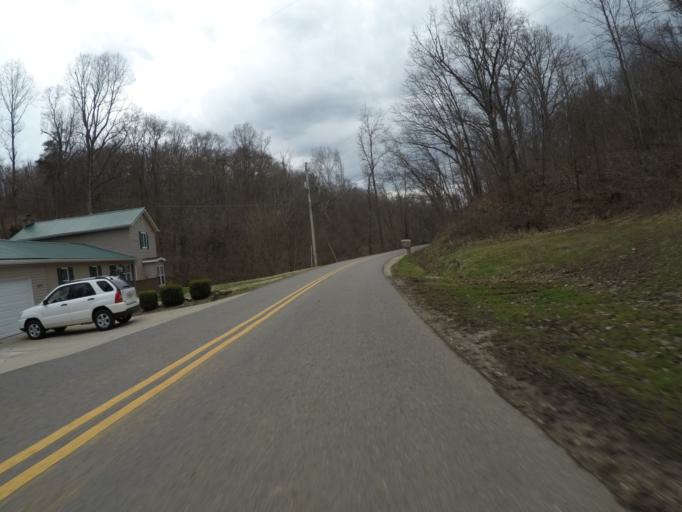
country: US
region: Ohio
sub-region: Lawrence County
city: Burlington
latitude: 38.4518
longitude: -82.5291
